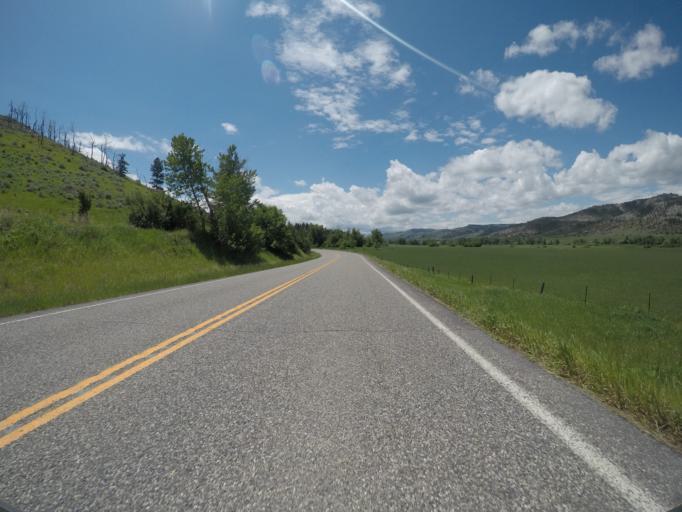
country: US
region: Montana
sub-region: Sweet Grass County
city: Big Timber
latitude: 45.6985
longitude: -110.0205
